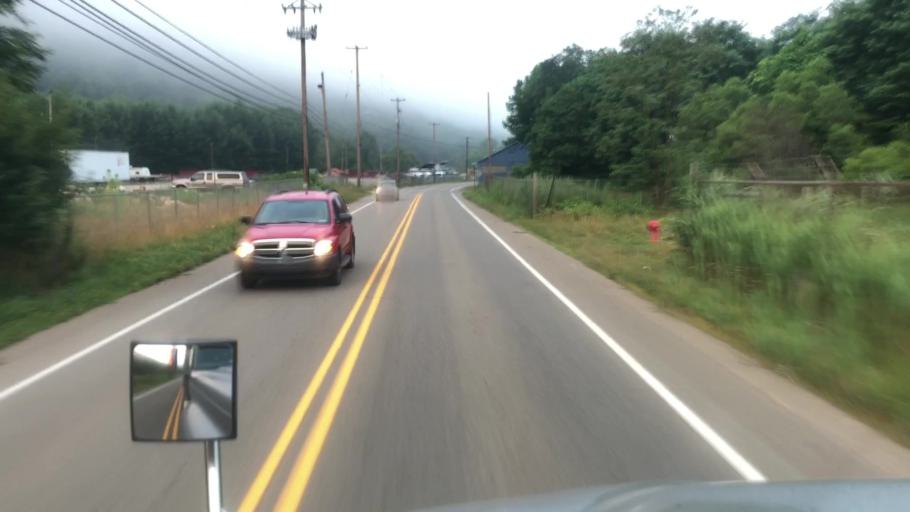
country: US
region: Pennsylvania
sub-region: Venango County
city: Hasson Heights
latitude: 41.4470
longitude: -79.6919
